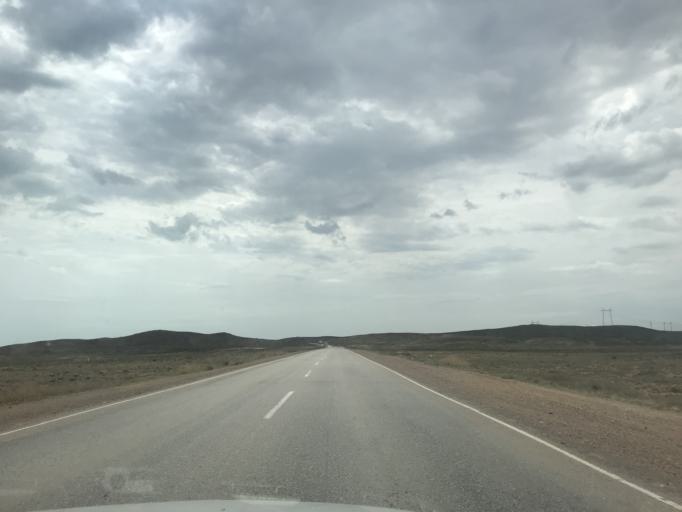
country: KZ
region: Zhambyl
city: Mynaral
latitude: 45.5147
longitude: 73.4941
